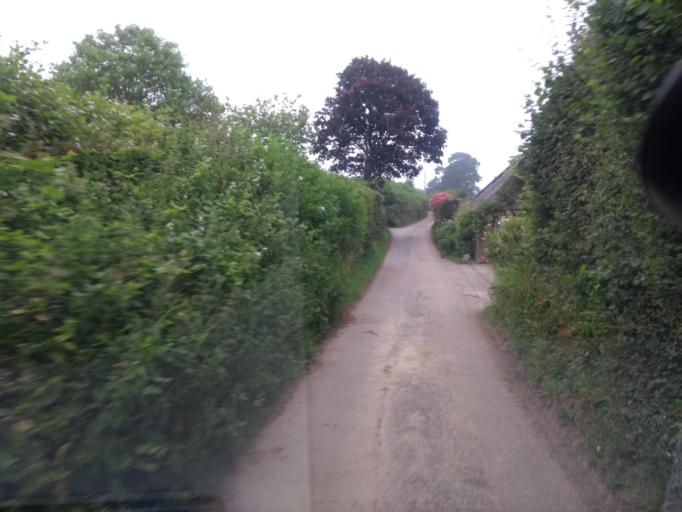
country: GB
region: England
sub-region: Dorset
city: Bridport
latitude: 50.7277
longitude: -2.7877
